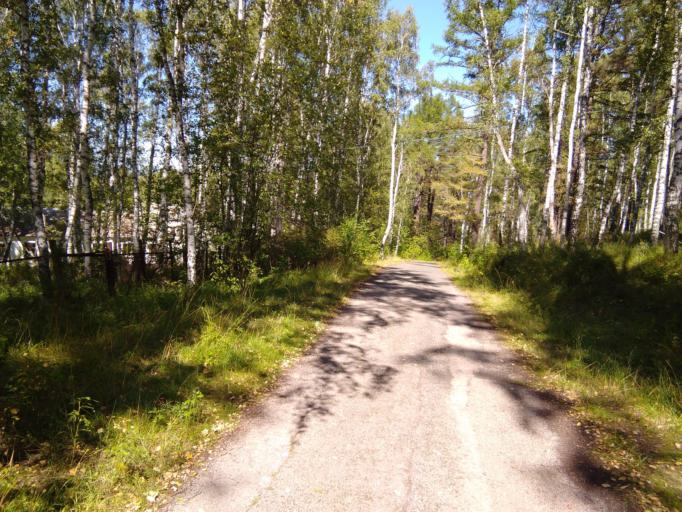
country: RU
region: Bashkortostan
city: Abzakovo
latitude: 53.8134
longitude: 58.6032
